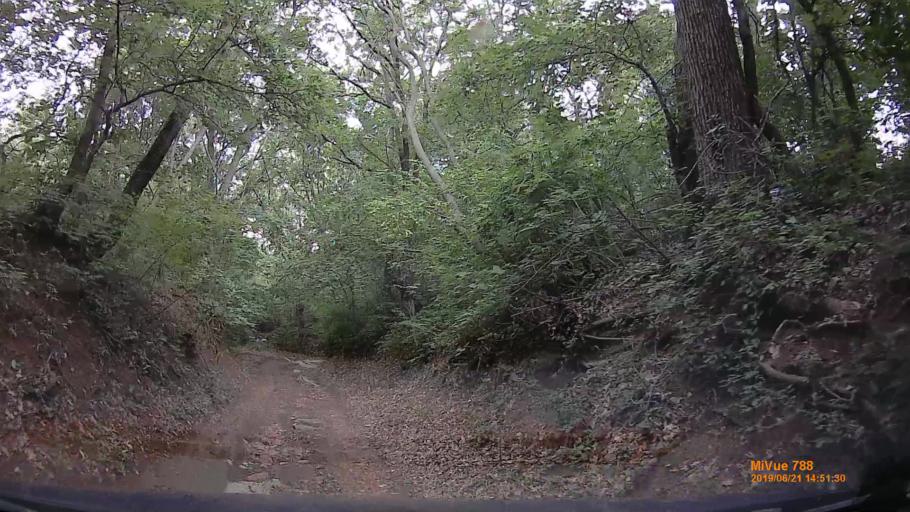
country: HU
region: Baranya
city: Hosszuheteny
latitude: 46.1293
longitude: 18.3101
